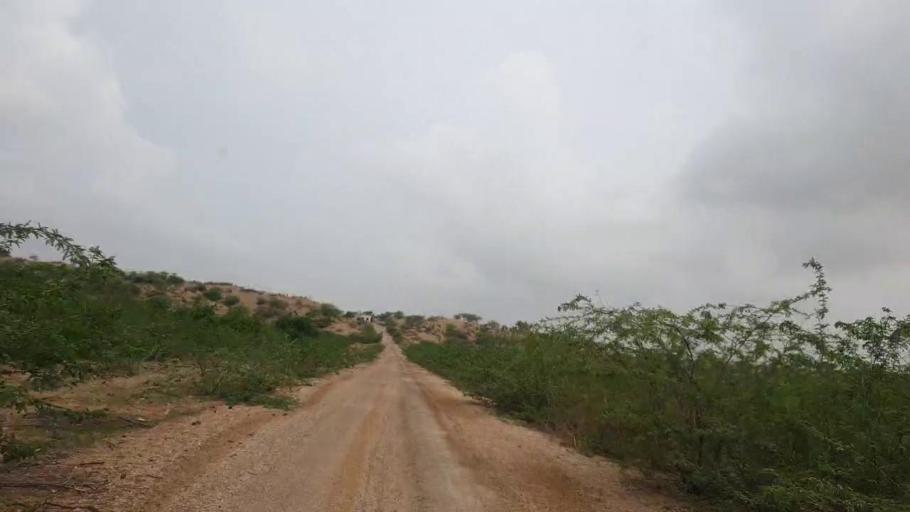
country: PK
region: Sindh
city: Diplo
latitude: 24.5559
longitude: 69.4563
